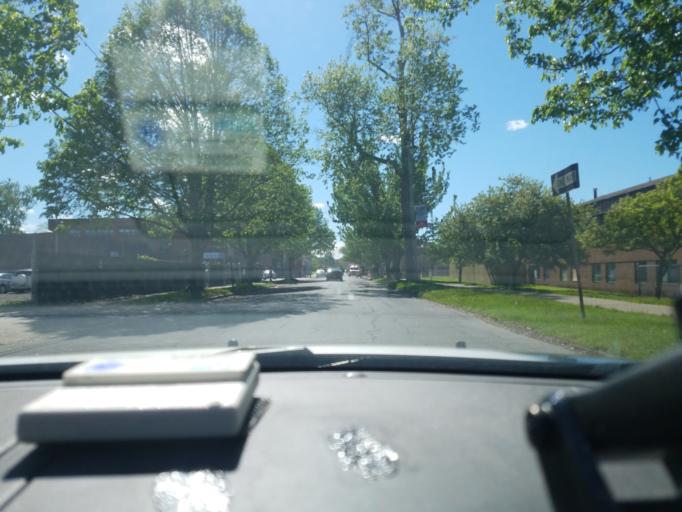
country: US
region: New York
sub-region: Onondaga County
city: Syracuse
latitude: 43.0436
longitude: -76.1545
